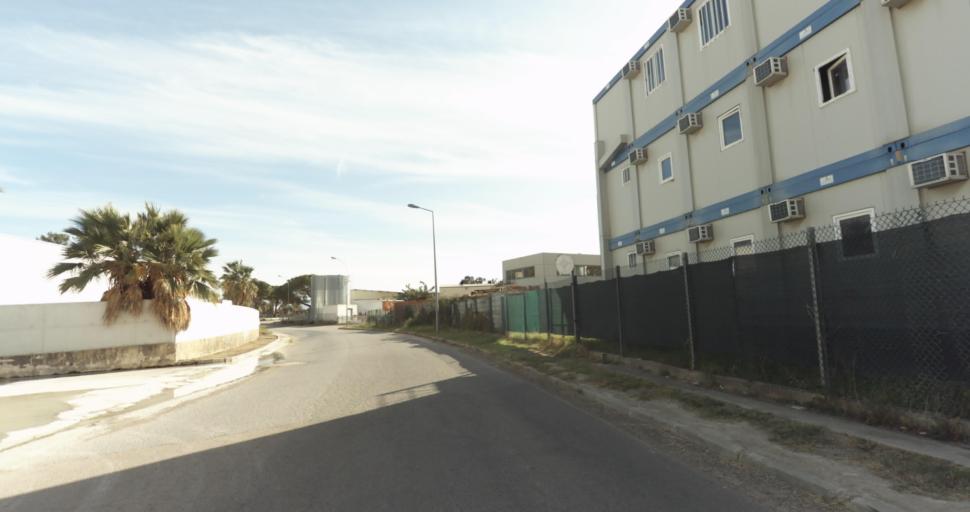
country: FR
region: Corsica
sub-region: Departement de la Corse-du-Sud
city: Afa
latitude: 41.9319
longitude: 8.7871
